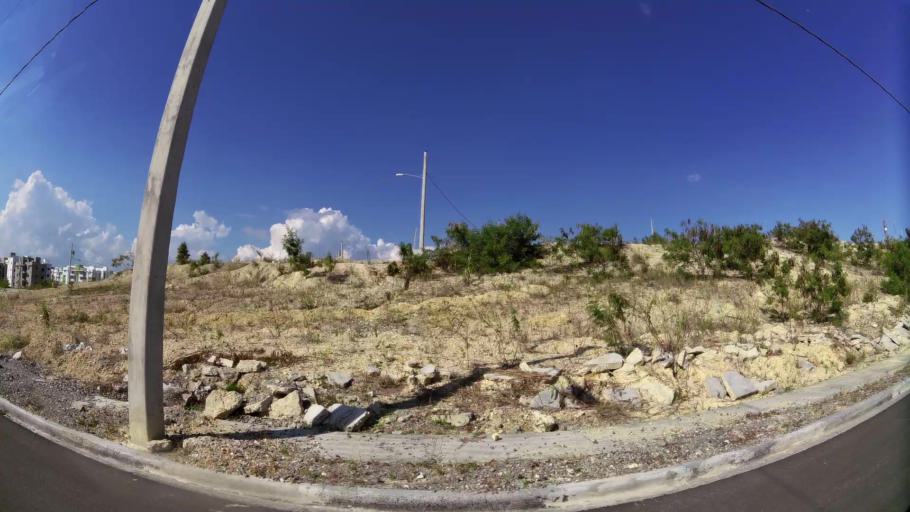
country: DO
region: Nacional
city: Santo Domingo
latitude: 18.4608
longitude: -69.9860
